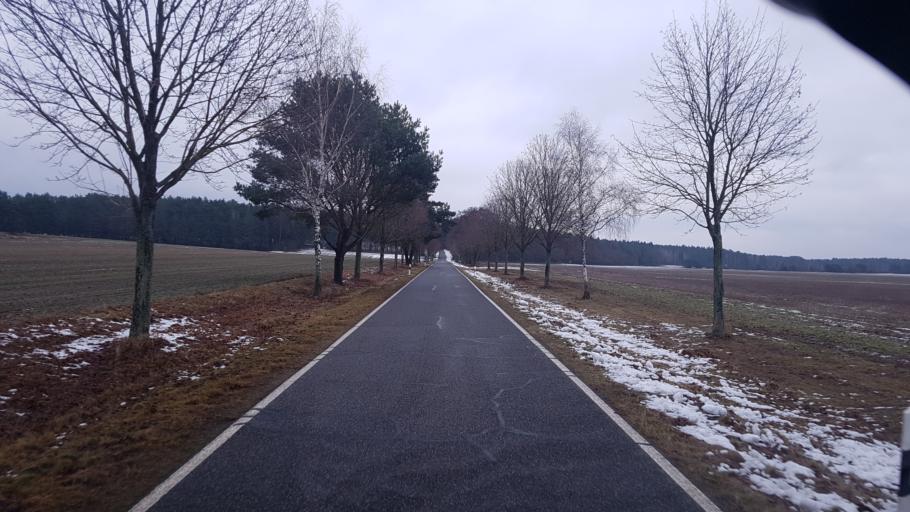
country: DE
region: Brandenburg
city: Jamlitz
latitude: 52.0201
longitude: 14.4340
